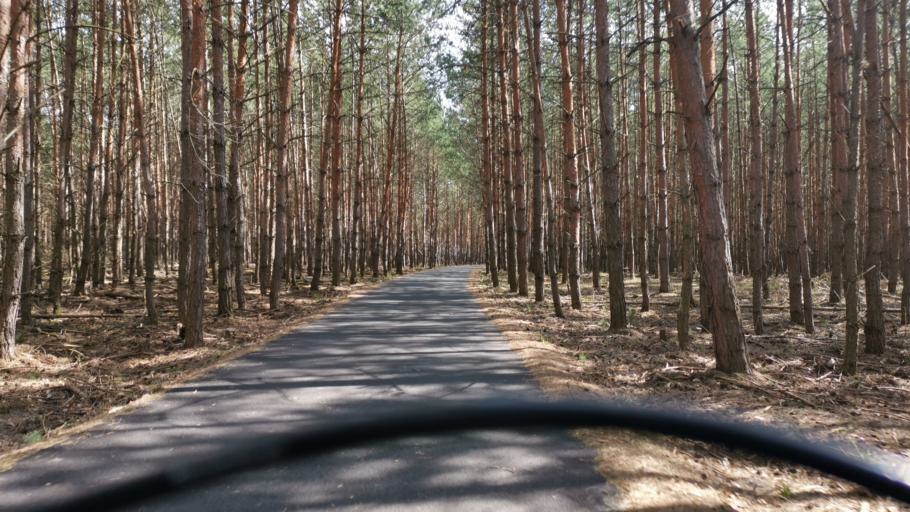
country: CZ
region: South Moravian
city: Tvrdonice
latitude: 48.7213
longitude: 17.0482
